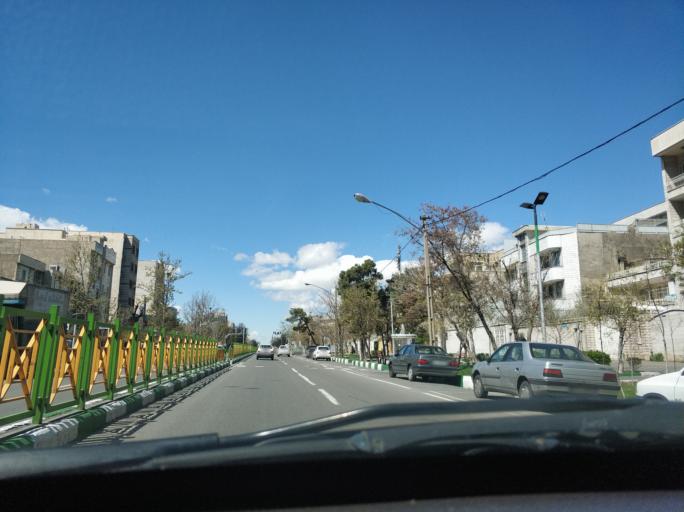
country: IR
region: Tehran
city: Tehran
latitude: 35.7201
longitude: 51.4940
